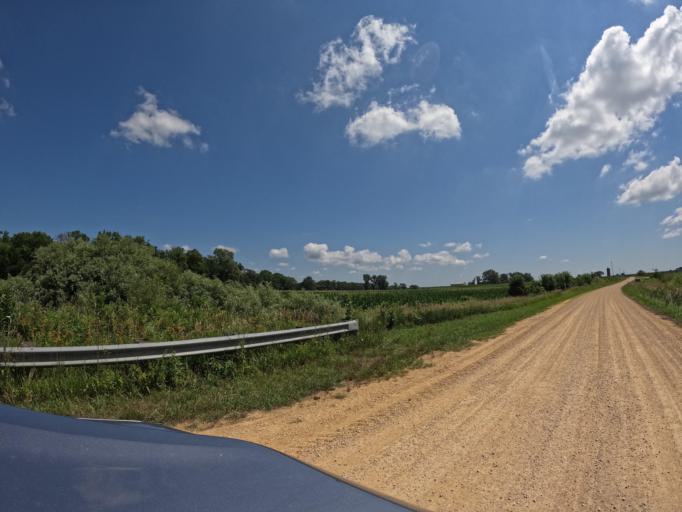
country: US
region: Iowa
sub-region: Clinton County
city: De Witt
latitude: 41.7811
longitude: -90.4303
